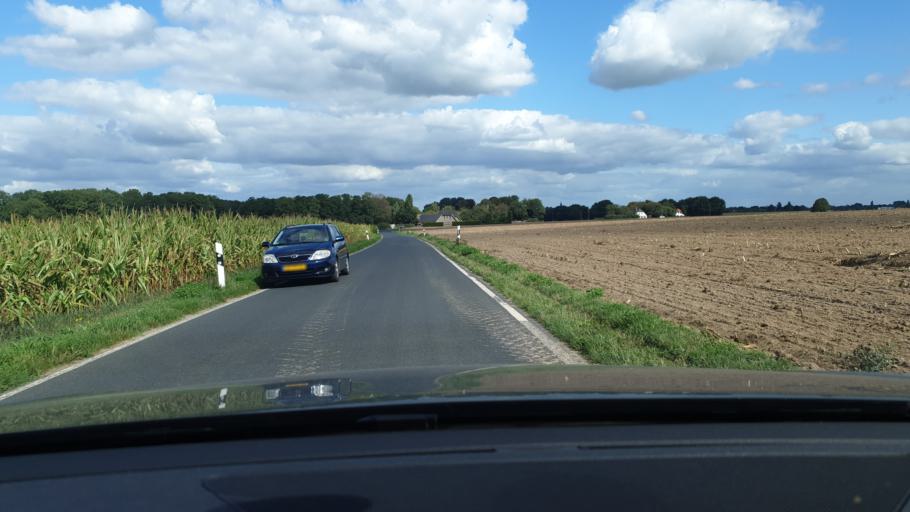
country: NL
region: Gelderland
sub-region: Gemeente Groesbeek
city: De Horst
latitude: 51.7719
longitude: 5.9928
